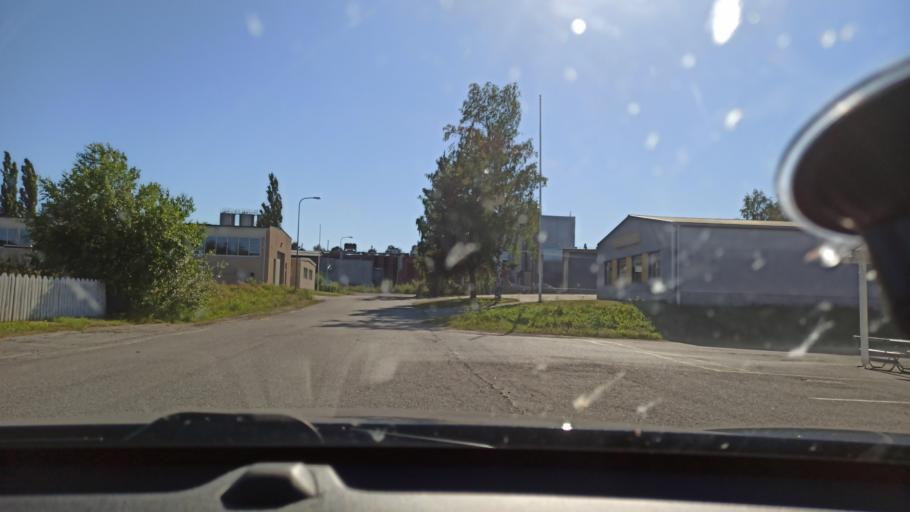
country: FI
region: Ostrobothnia
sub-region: Jakobstadsregionen
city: Jakobstad
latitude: 63.6873
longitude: 22.7074
